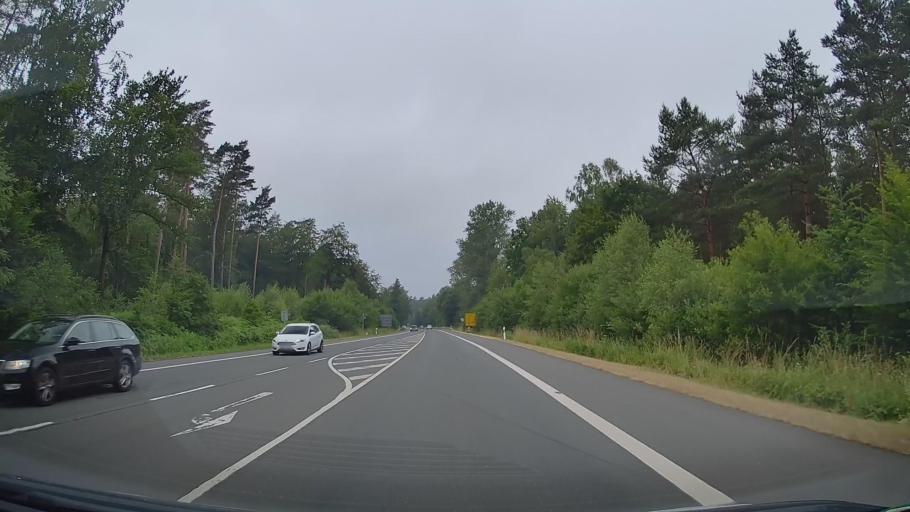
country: DE
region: North Rhine-Westphalia
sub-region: Regierungsbezirk Detmold
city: Hille
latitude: 52.3953
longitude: 8.7035
